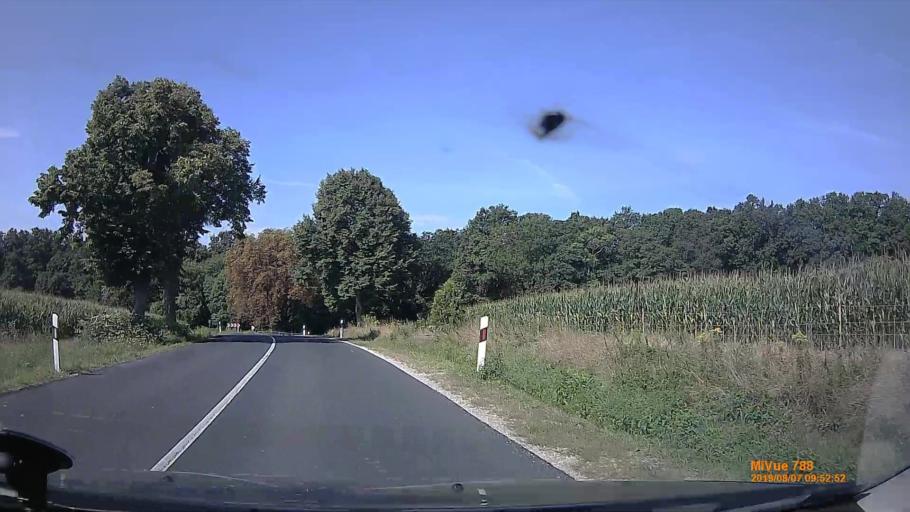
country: HU
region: Zala
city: Zalaegerszeg
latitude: 46.7317
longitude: 16.8877
